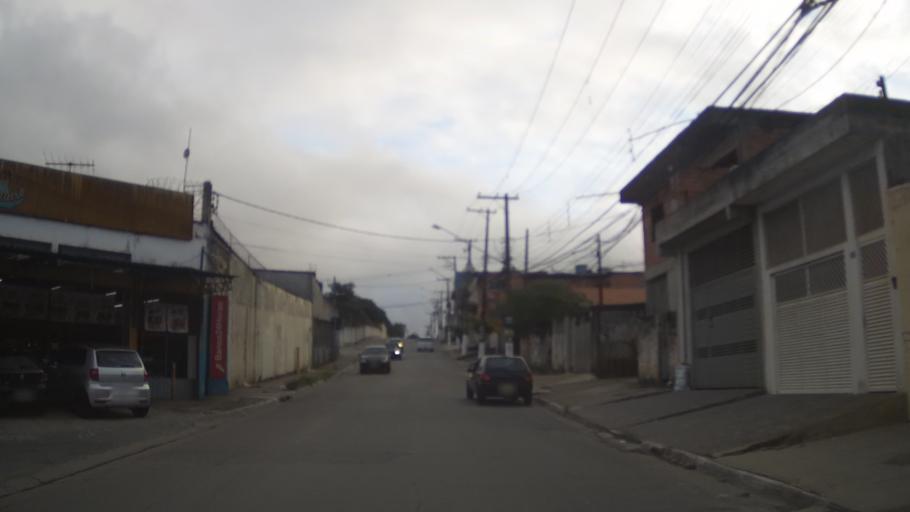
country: BR
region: Sao Paulo
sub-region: Itaquaquecetuba
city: Itaquaquecetuba
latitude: -23.4426
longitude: -46.4267
